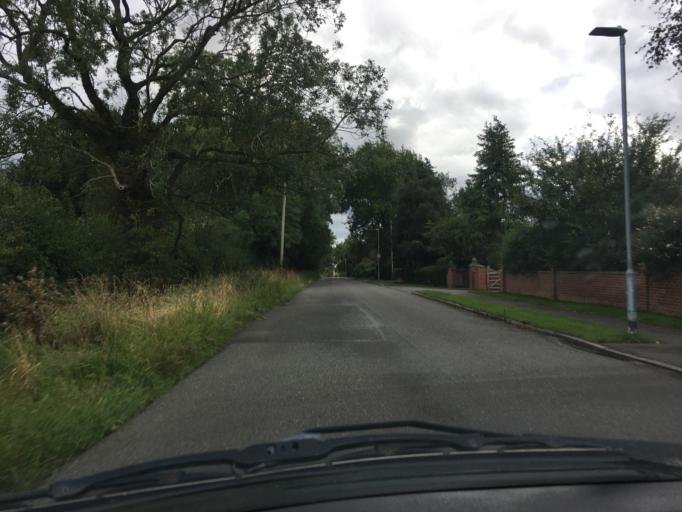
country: GB
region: England
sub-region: Leicestershire
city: Lutterworth
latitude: 52.4733
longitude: -1.2100
